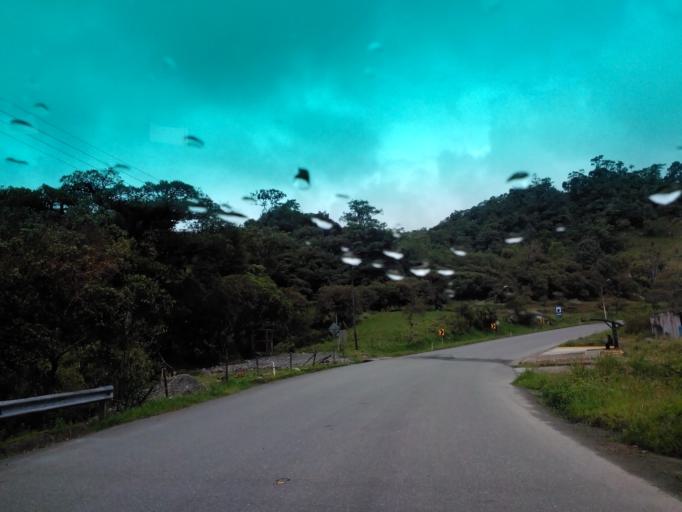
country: EC
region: Napo
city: Archidona
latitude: -0.5806
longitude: -77.8657
